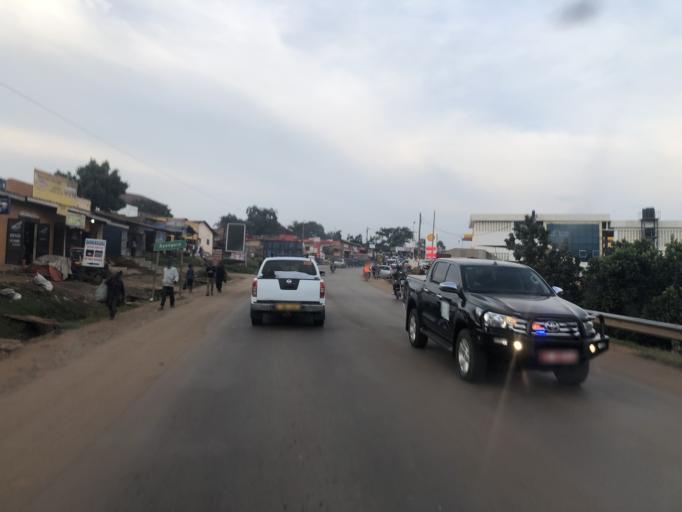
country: UG
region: Central Region
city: Kampala Central Division
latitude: 0.2898
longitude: 32.4981
